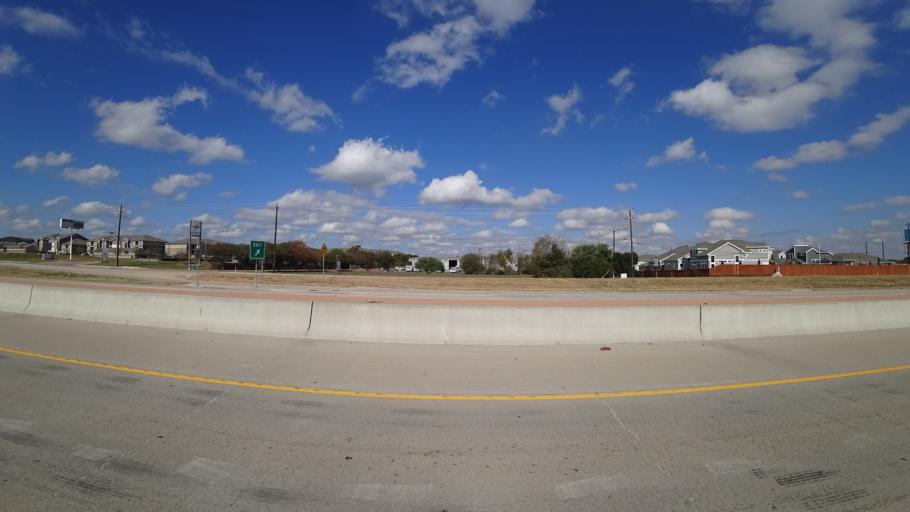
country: US
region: Texas
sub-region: Travis County
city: Austin
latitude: 30.2153
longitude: -97.6998
